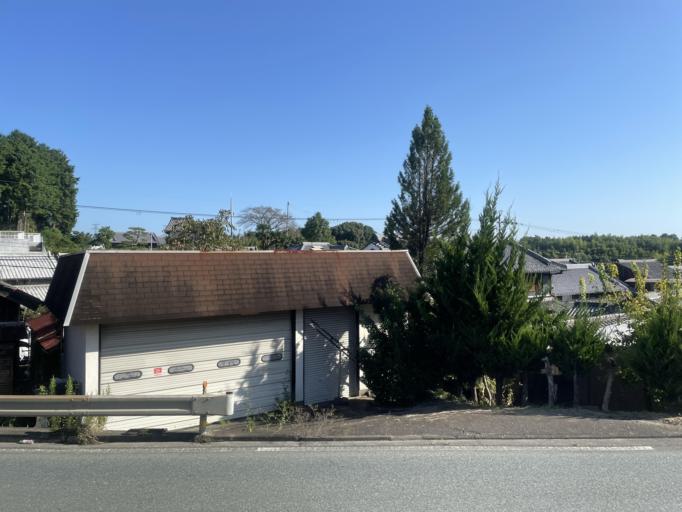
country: JP
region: Osaka
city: Kashihara
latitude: 34.5412
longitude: 135.6797
